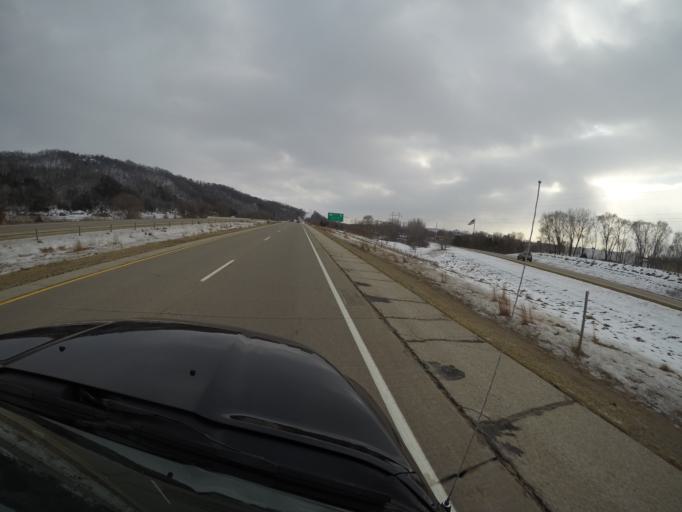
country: US
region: Wisconsin
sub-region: La Crosse County
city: Onalaska
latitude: 43.8993
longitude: -91.2218
